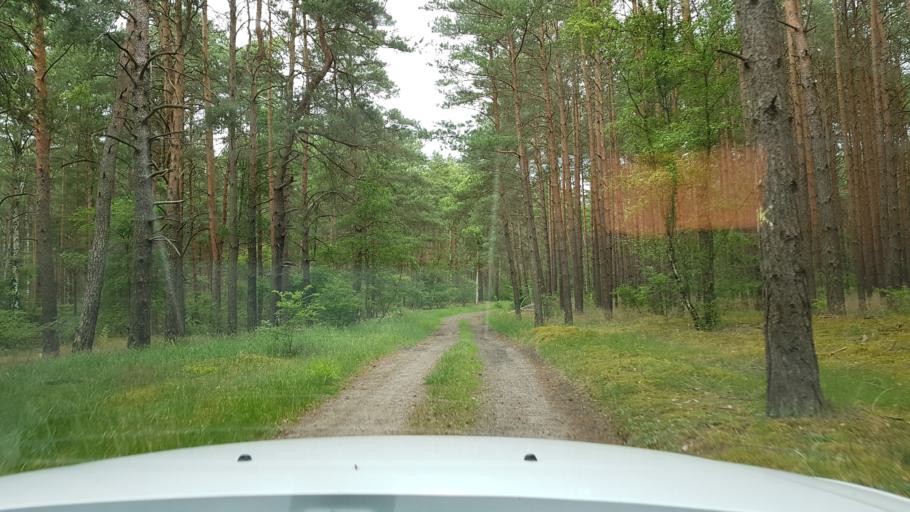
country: PL
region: West Pomeranian Voivodeship
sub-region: Powiat mysliborski
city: Boleszkowice
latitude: 52.6568
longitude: 14.5684
